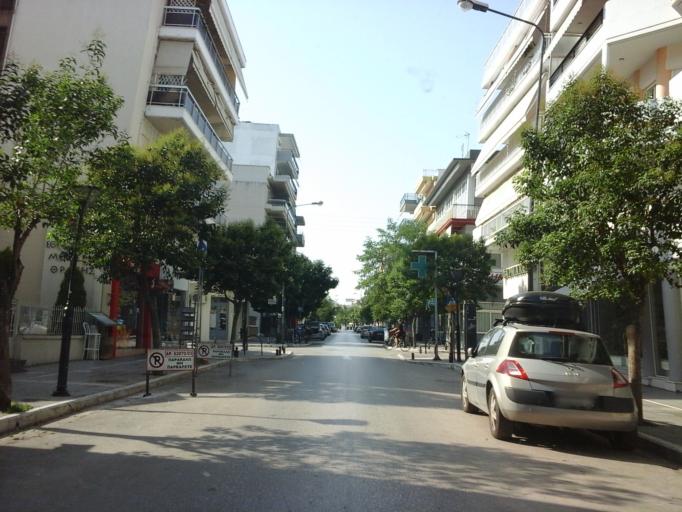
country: GR
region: East Macedonia and Thrace
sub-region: Nomos Evrou
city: Alexandroupoli
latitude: 40.8481
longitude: 25.8745
